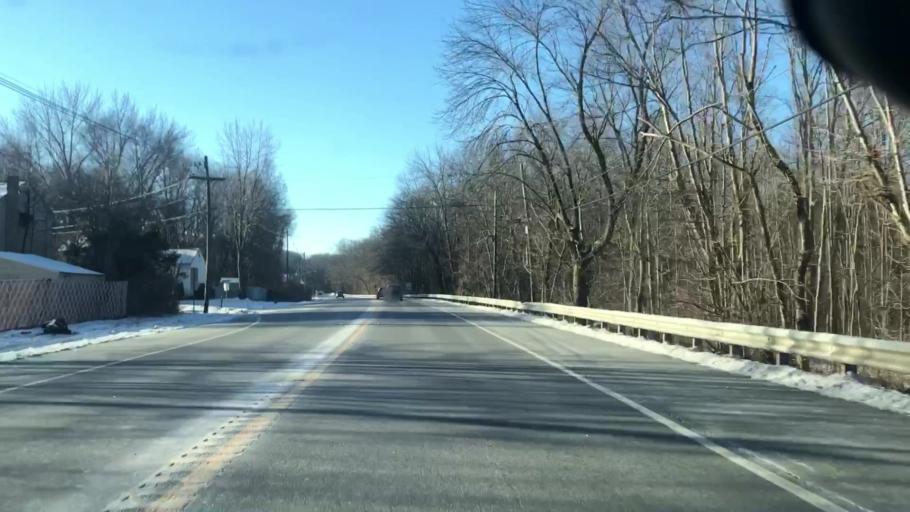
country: US
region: New Jersey
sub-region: Morris County
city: Chester
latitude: 40.8187
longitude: -74.7108
